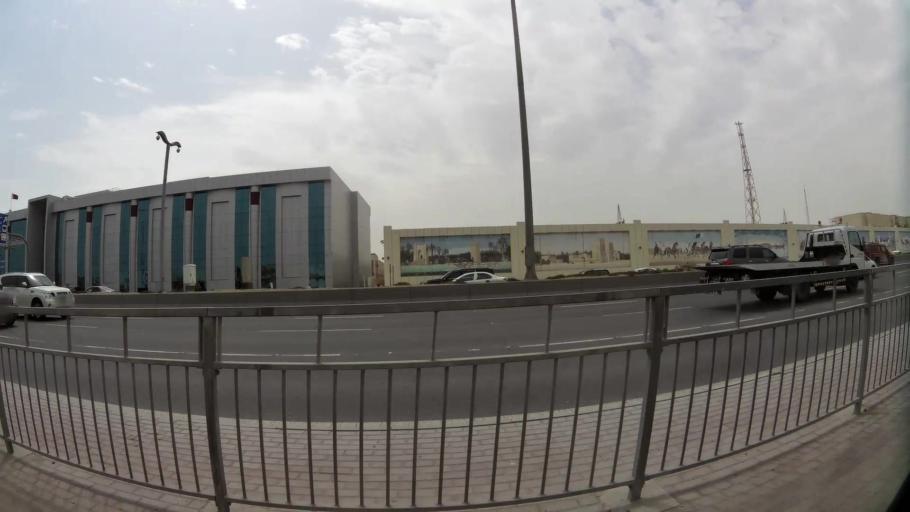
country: QA
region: Baladiyat ar Rayyan
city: Ar Rayyan
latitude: 25.3287
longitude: 51.4660
